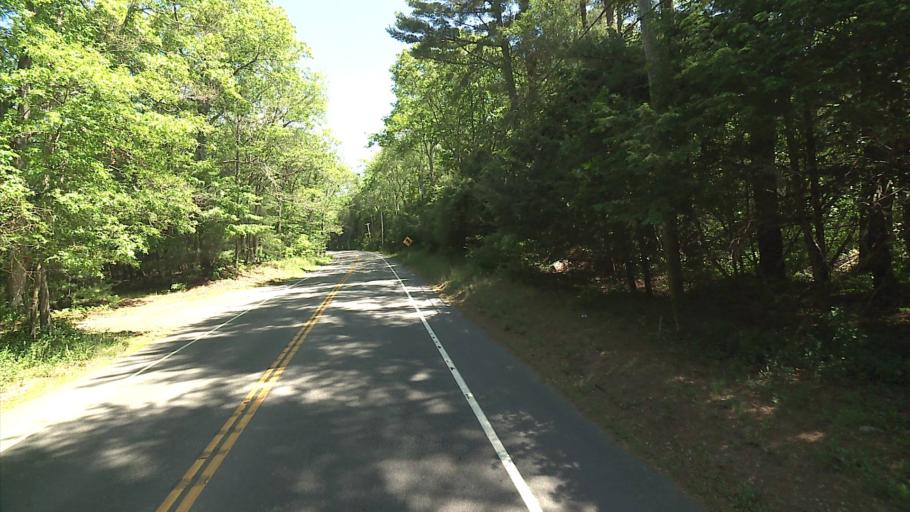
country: US
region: Rhode Island
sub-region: Washington County
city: Hopkinton
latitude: 41.5292
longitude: -71.8369
